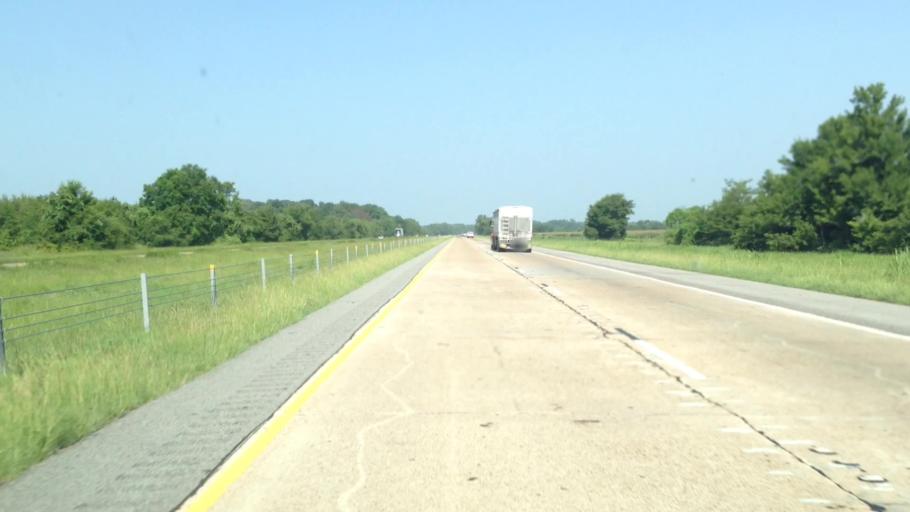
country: US
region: Mississippi
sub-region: Warren County
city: Vicksburg
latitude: 32.3325
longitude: -91.0397
